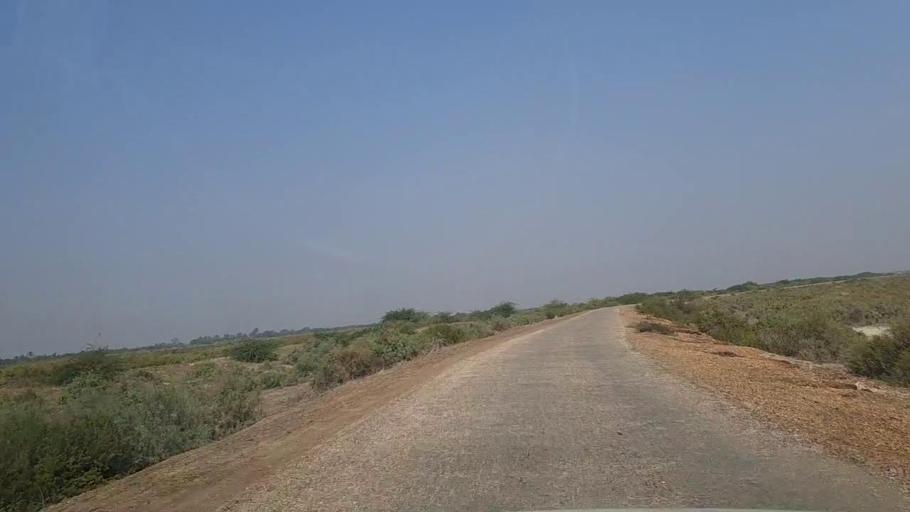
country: PK
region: Sindh
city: Keti Bandar
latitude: 24.2300
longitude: 67.6755
